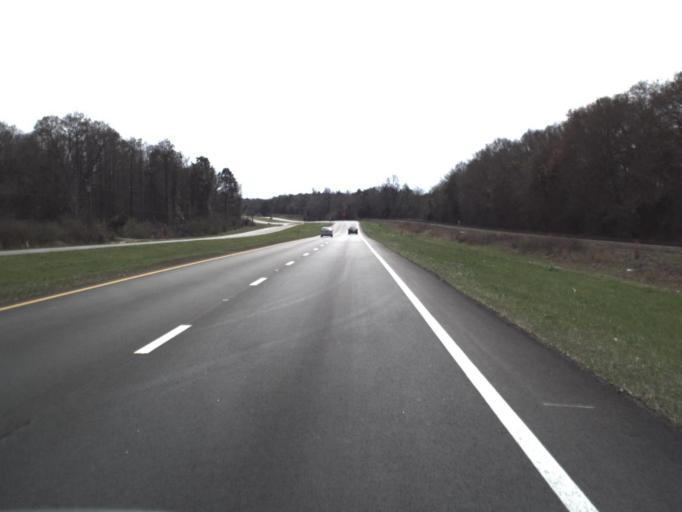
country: US
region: Florida
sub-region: Washington County
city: Chipley
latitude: 30.6784
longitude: -85.3940
